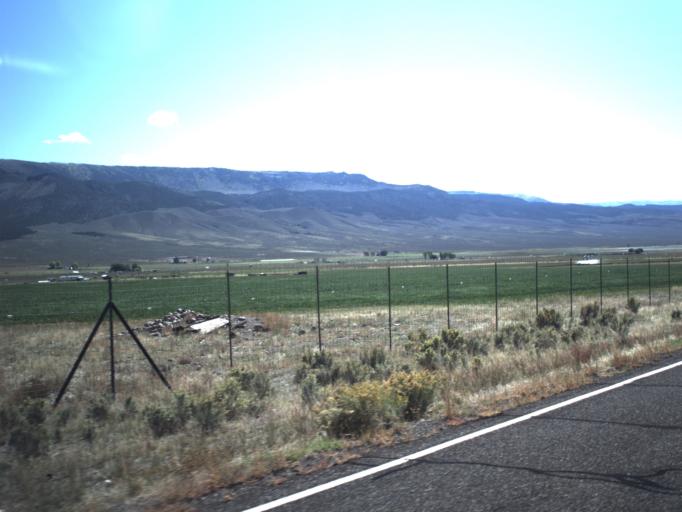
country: US
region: Utah
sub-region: Piute County
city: Junction
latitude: 38.2675
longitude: -111.9865
